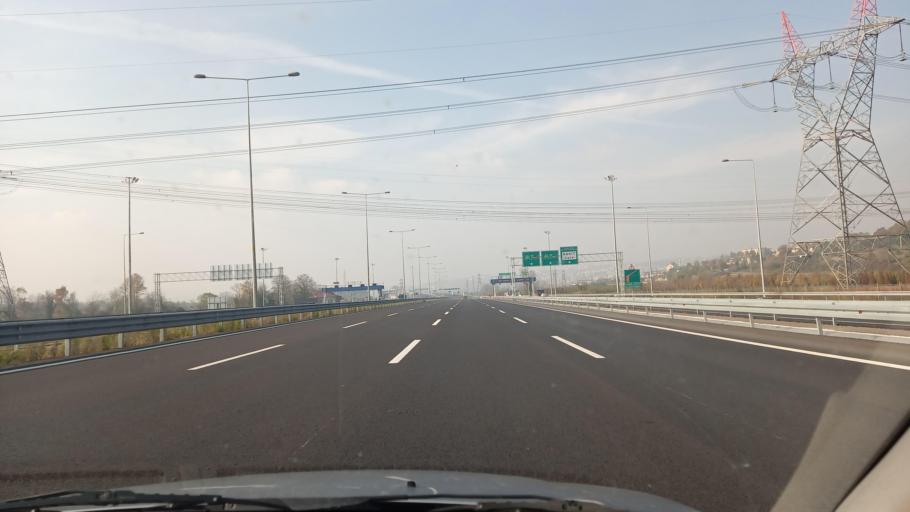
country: TR
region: Sakarya
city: Kazimpasa
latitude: 40.8423
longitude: 30.3460
